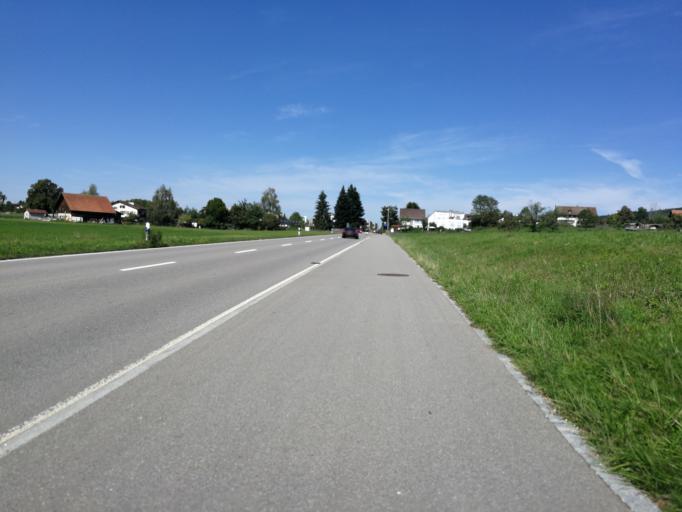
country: CH
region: Zurich
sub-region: Bezirk Hinwil
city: Hinwil
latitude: 47.2919
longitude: 8.8426
